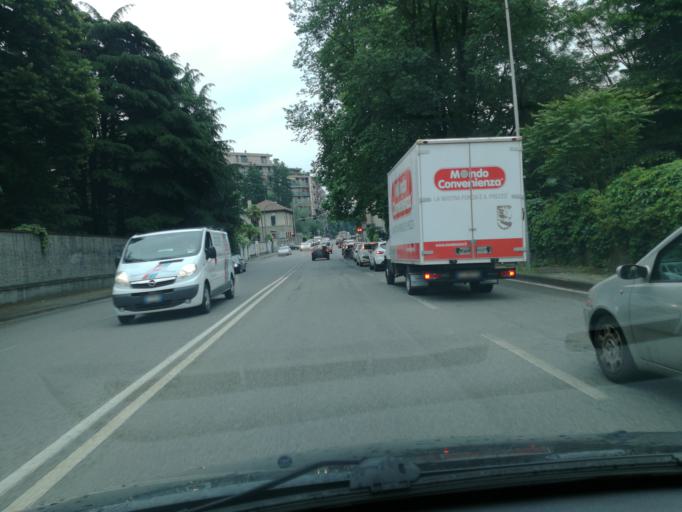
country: IT
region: Lombardy
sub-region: Provincia di Monza e Brianza
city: Monza
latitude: 45.5903
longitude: 9.2818
